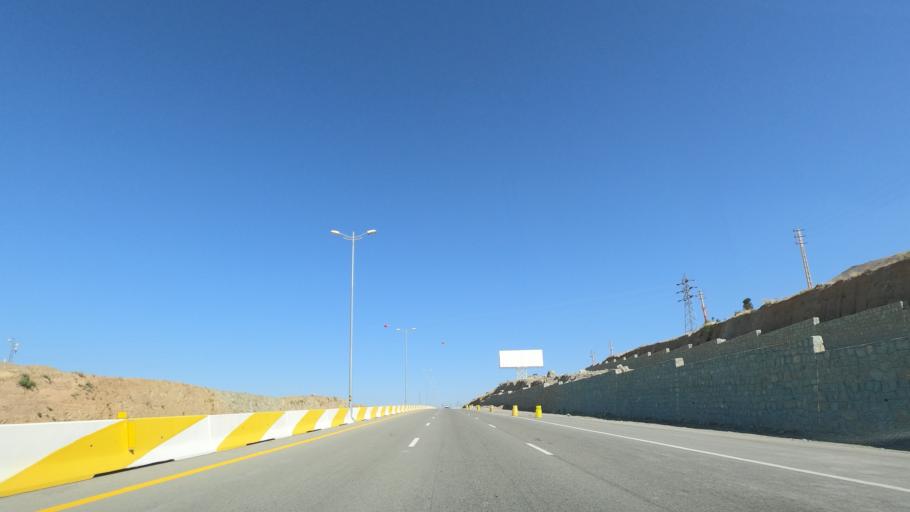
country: IR
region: Tehran
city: Shahr-e Qods
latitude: 35.7653
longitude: 51.0686
